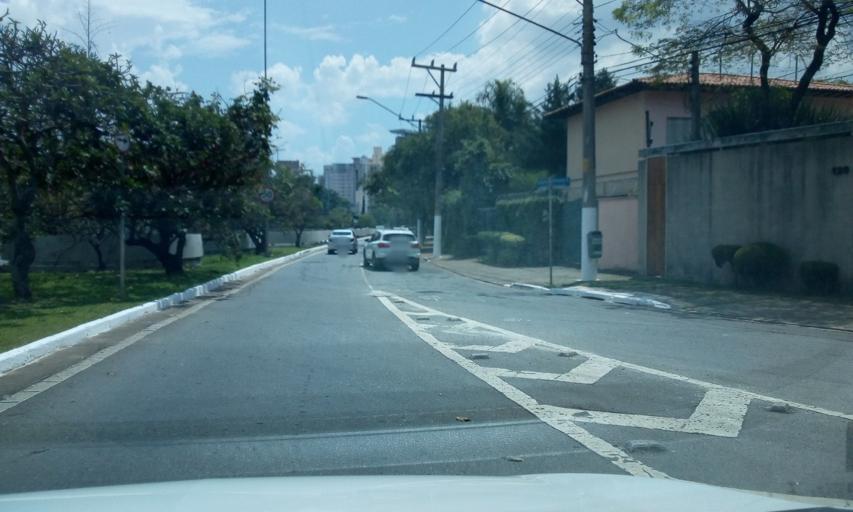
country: BR
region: Sao Paulo
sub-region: Sao Paulo
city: Sao Paulo
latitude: -23.5872
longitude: -46.6653
